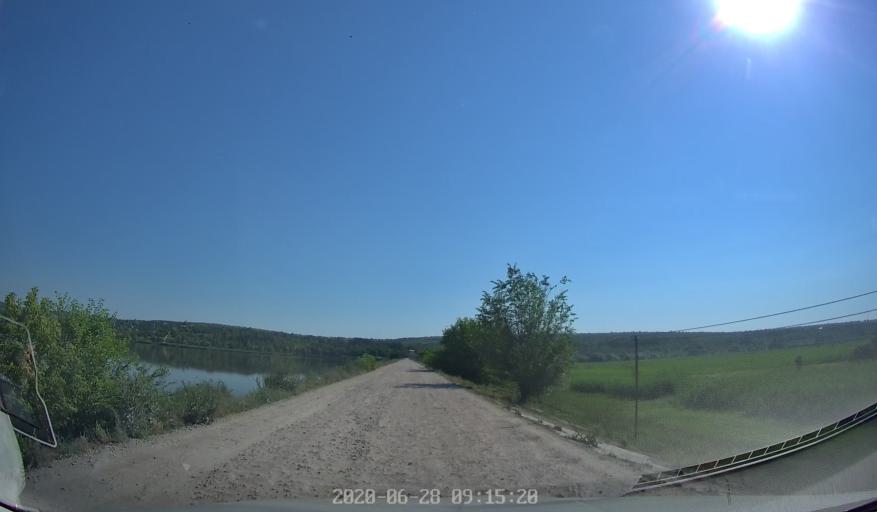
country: MD
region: Laloveni
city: Ialoveni
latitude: 46.9767
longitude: 28.6978
